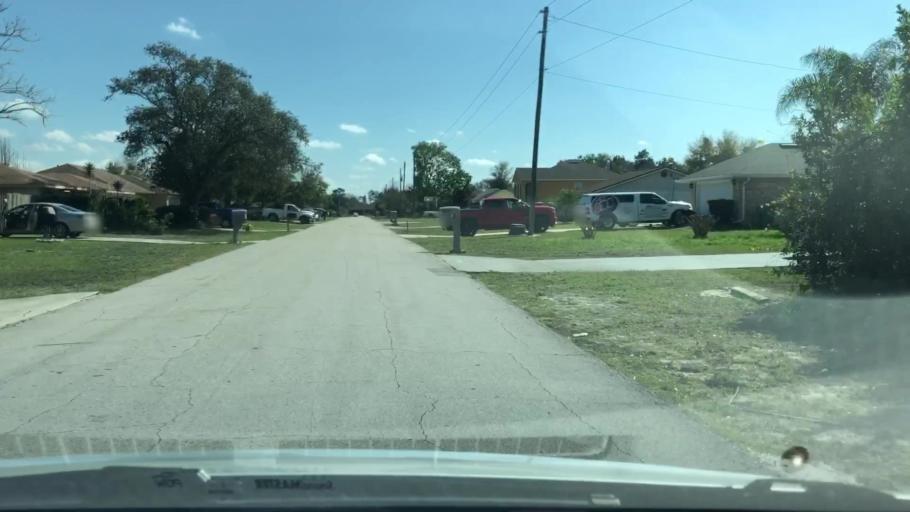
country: US
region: Florida
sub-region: Volusia County
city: Deltona
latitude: 28.8798
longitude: -81.2415
